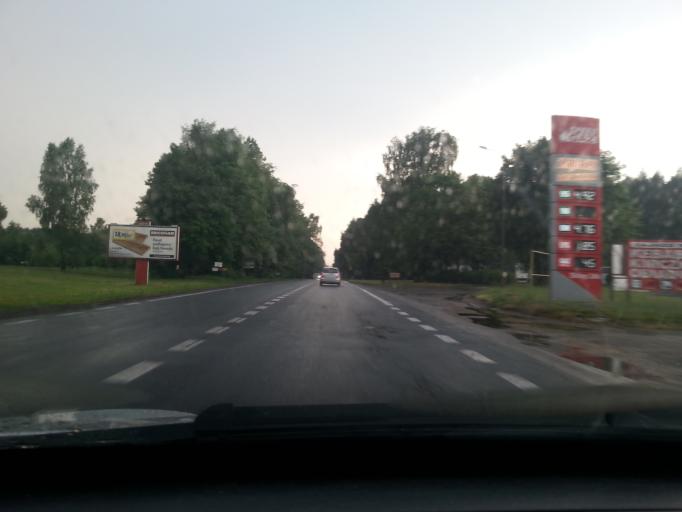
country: PL
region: Lodz Voivodeship
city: Lodz
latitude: 51.8240
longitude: 19.5175
